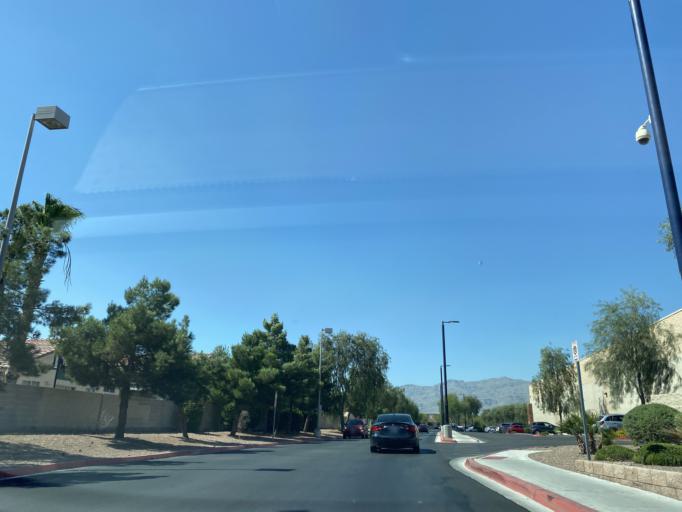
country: US
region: Nevada
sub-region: Clark County
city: North Las Vegas
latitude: 36.2691
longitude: -115.2090
